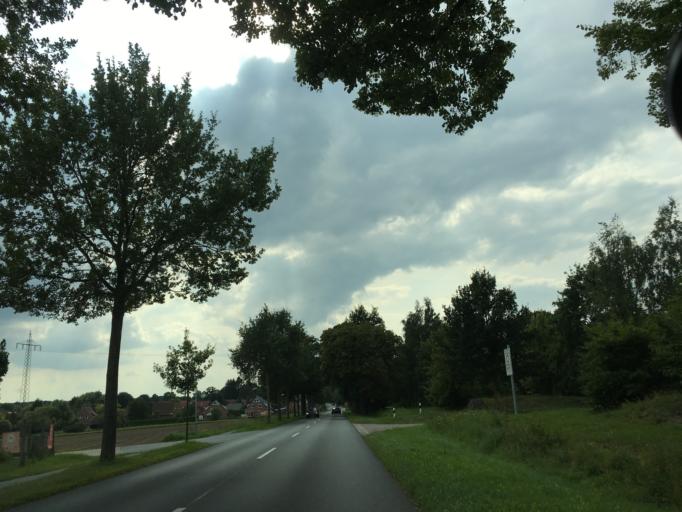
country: DE
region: Lower Saxony
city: Melbeck
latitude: 53.2175
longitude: 10.3776
